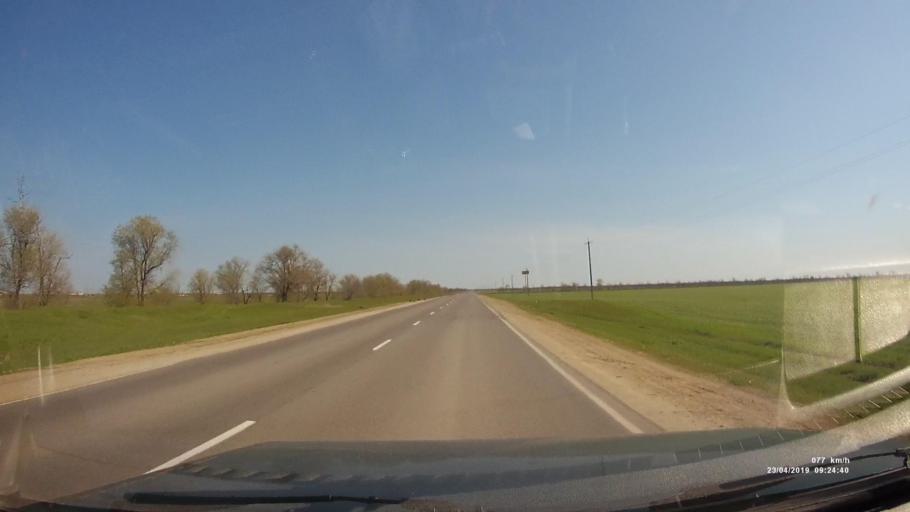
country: RU
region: Rostov
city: Proletarsk
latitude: 46.7072
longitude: 41.7560
